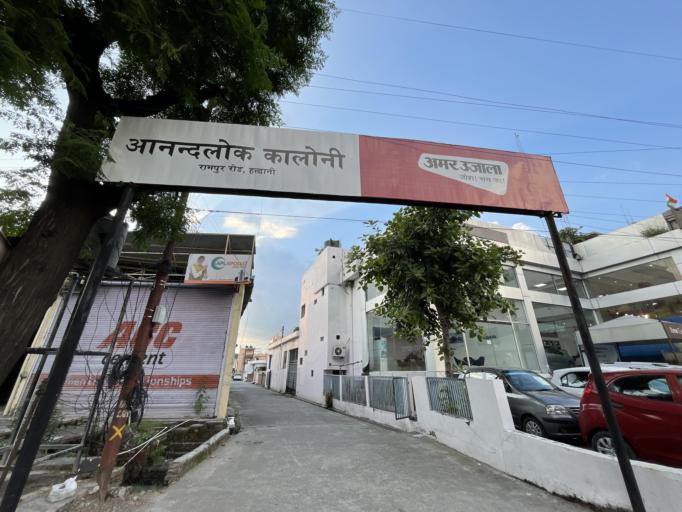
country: IN
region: Uttarakhand
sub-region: Naini Tal
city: Haldwani
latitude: 29.1905
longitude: 79.5050
